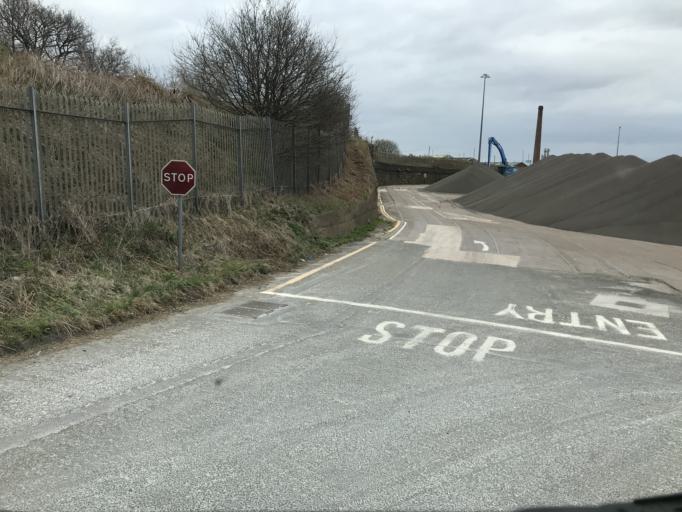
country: GB
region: England
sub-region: Cheshire West and Chester
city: Ellesmere Port
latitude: 53.3502
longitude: -2.9029
